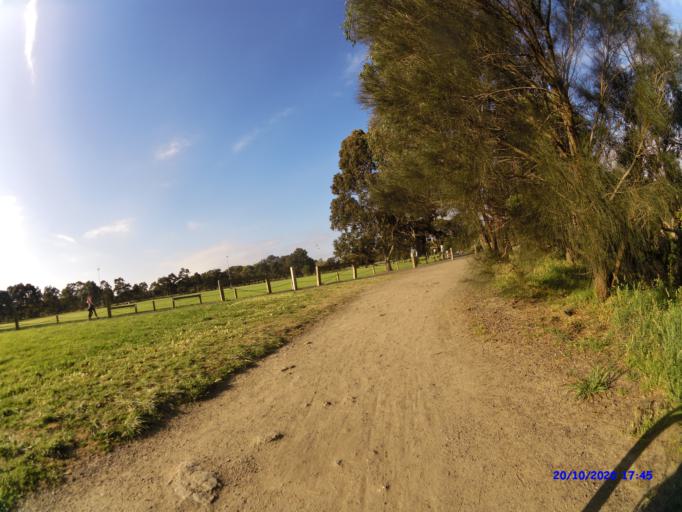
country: AU
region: Victoria
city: Abbotsford
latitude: -37.7959
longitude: 145.0075
